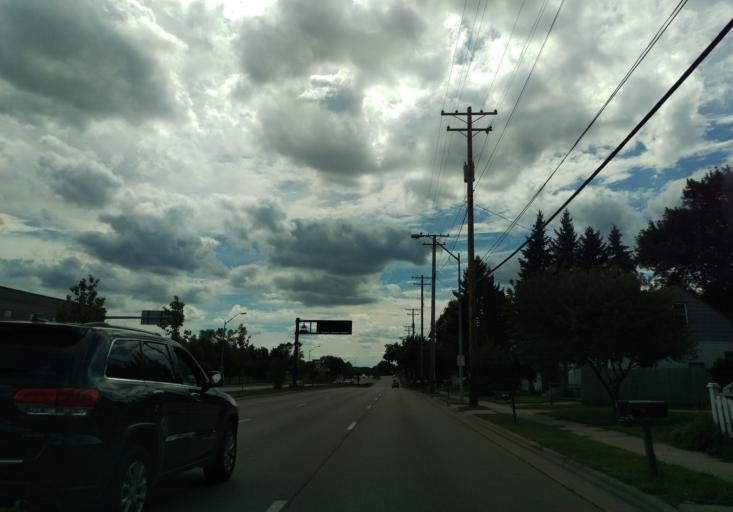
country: US
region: Wisconsin
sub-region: Dane County
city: Maple Bluff
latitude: 43.1211
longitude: -89.3551
